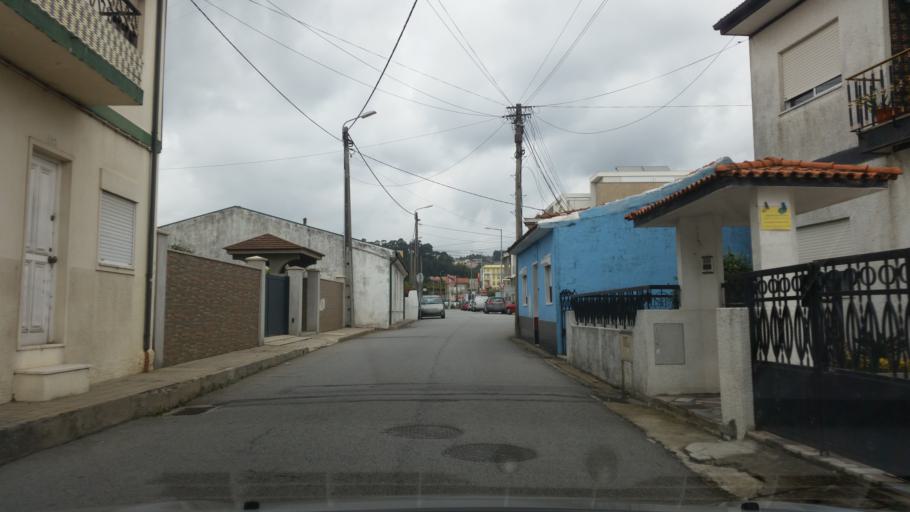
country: PT
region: Porto
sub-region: Valongo
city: Alfena
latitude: 41.2365
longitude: -8.5329
